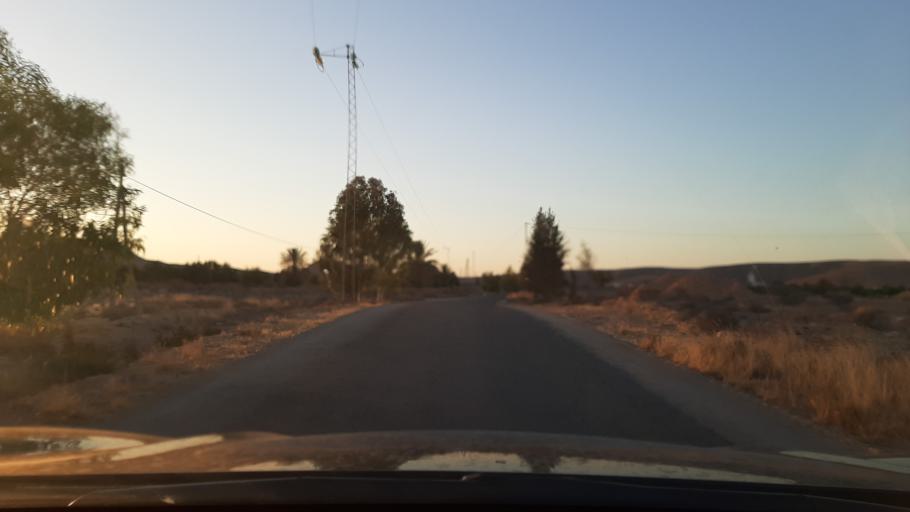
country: TN
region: Qabis
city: Matmata
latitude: 33.5641
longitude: 10.1798
